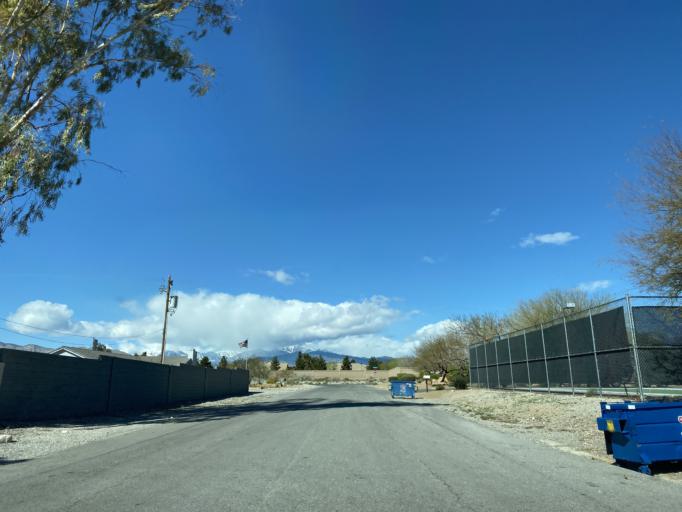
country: US
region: Nevada
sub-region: Clark County
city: North Las Vegas
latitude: 36.3267
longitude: -115.2862
